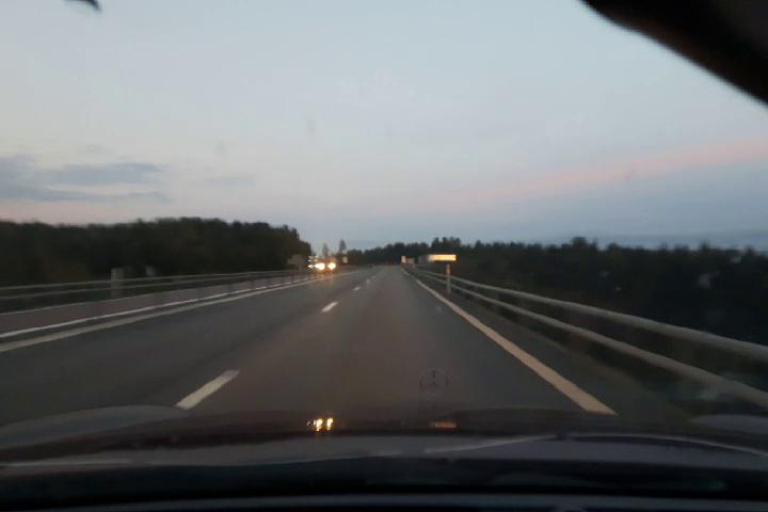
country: SE
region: Vaesternorrland
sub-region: Kramfors Kommun
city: Nordingra
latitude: 62.8791
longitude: 18.0780
